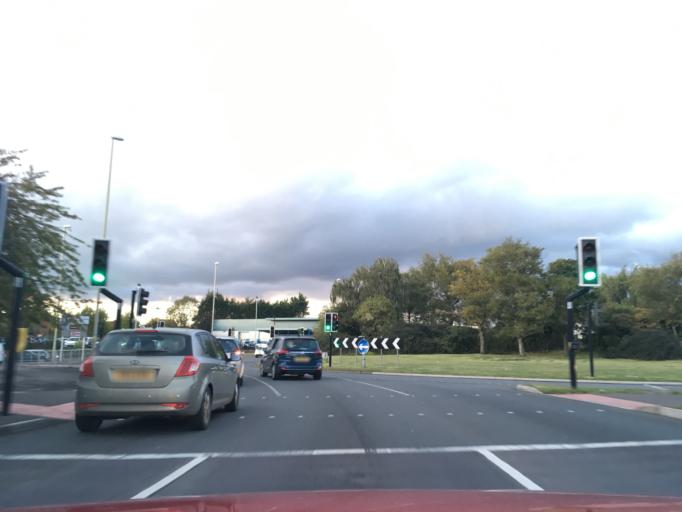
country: GB
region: England
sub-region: Gloucestershire
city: Barnwood
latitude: 51.8638
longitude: -2.2137
